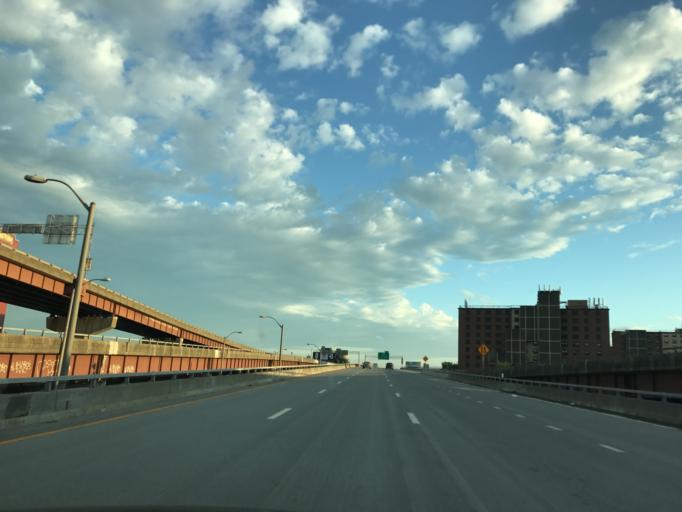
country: US
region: New York
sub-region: Rensselaer County
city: Rensselaer
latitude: 42.6424
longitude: -73.7518
